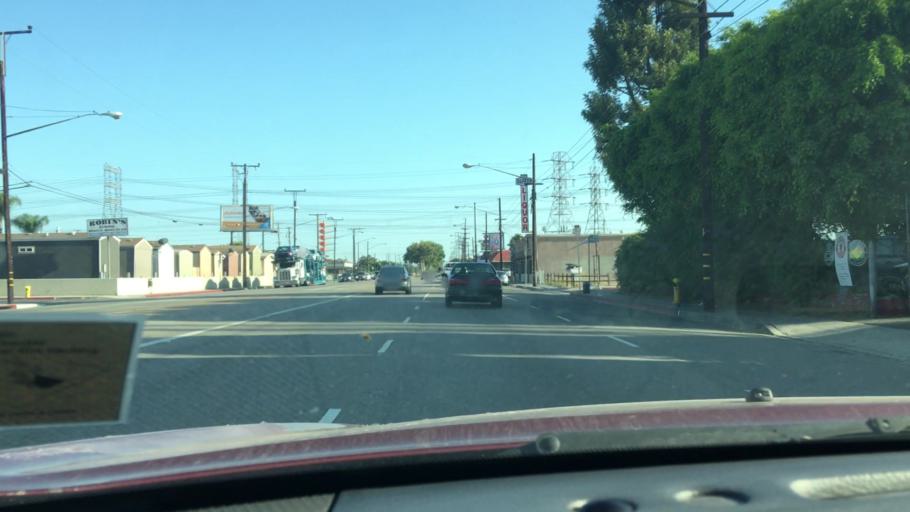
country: US
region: California
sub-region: Los Angeles County
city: Lakewood
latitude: 33.8716
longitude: -118.1427
